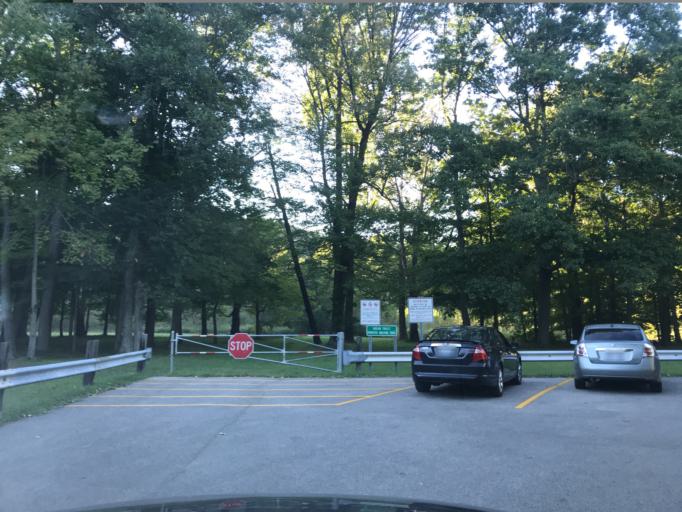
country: US
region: Ohio
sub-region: Ashtabula County
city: Edgewood
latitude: 41.8571
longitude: -80.7616
